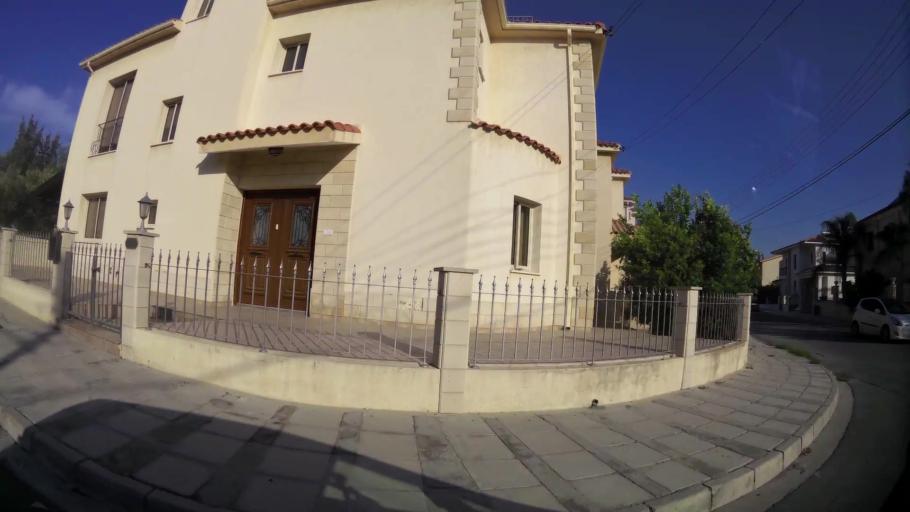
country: CY
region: Larnaka
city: Aradippou
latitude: 34.9375
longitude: 33.5949
